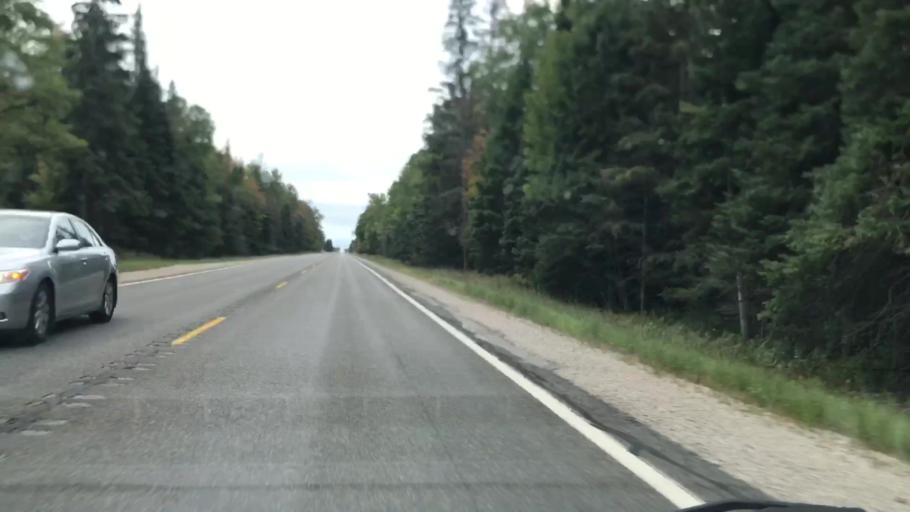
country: US
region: Michigan
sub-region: Luce County
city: Newberry
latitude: 46.2257
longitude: -85.5721
